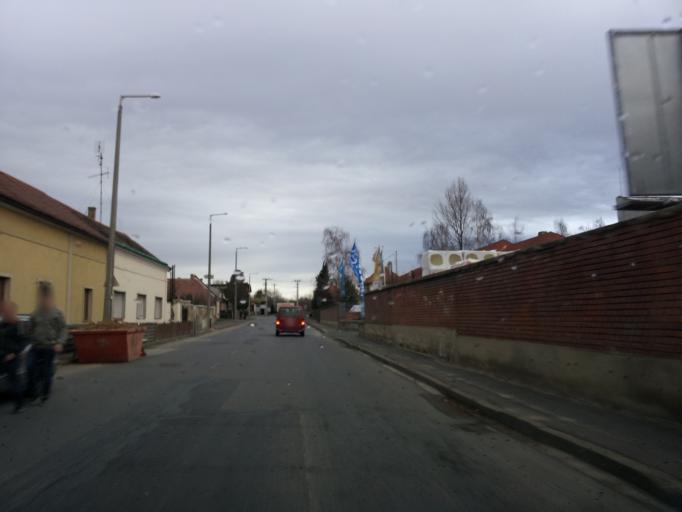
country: HU
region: Vas
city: Koszeg
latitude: 47.3819
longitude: 16.5553
